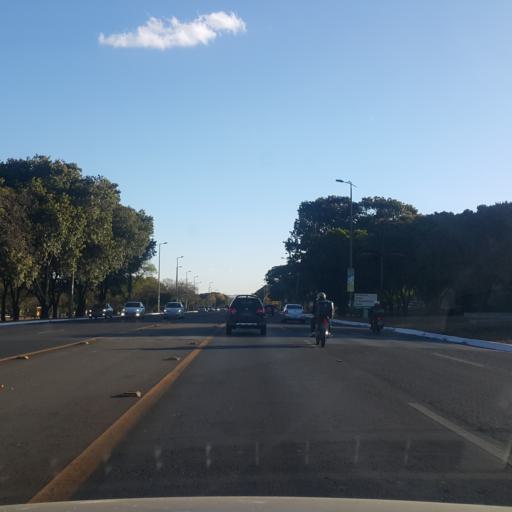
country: BR
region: Federal District
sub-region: Brasilia
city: Brasilia
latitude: -15.8268
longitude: -47.9143
